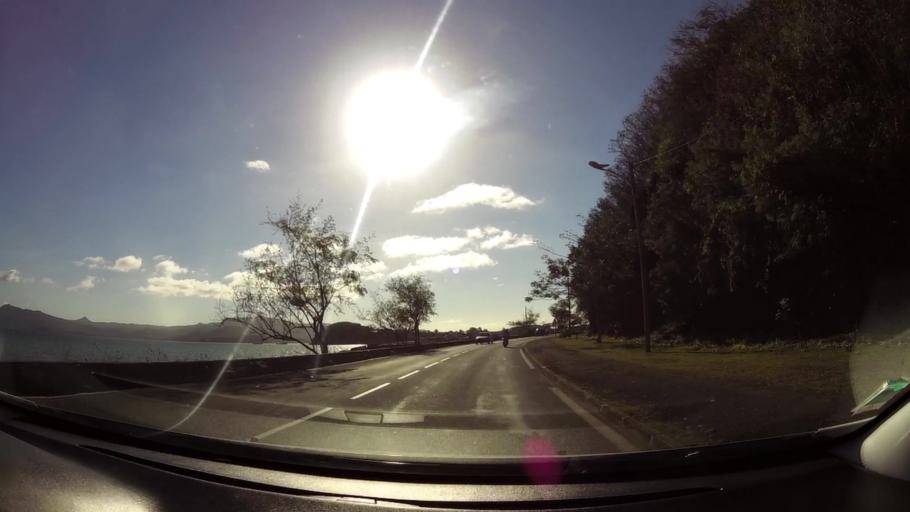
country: YT
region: Pamandzi
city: Pamandzi
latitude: -12.7912
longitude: 45.2683
